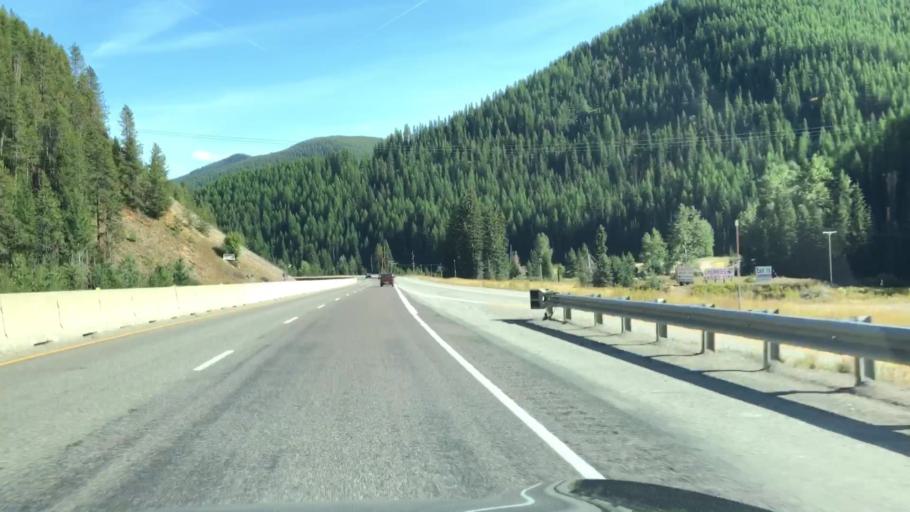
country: US
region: Montana
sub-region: Sanders County
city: Thompson Falls
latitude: 47.4211
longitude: -115.6049
